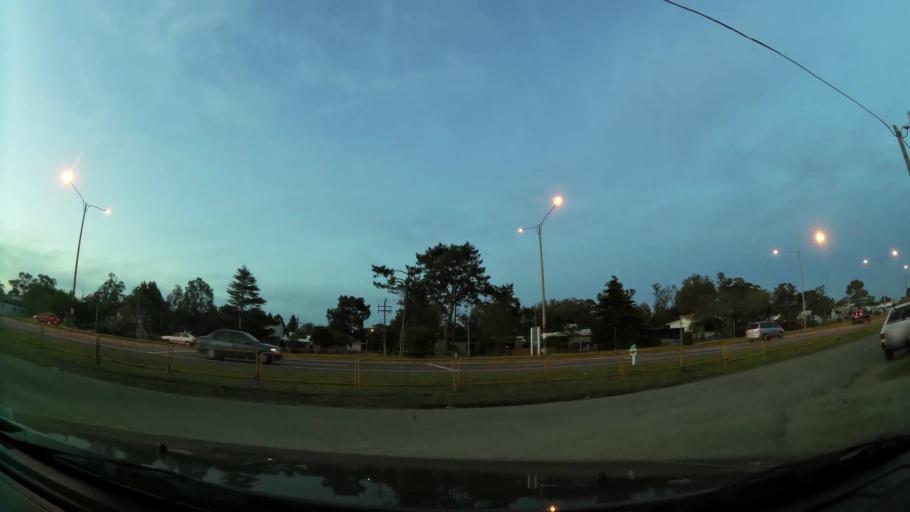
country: UY
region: Canelones
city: Atlantida
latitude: -34.7661
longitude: -55.7578
